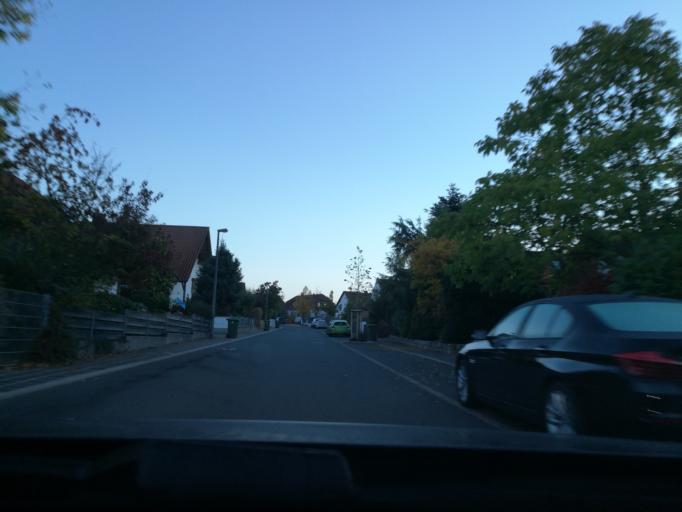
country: DE
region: Bavaria
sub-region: Regierungsbezirk Mittelfranken
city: Veitsbronn
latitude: 49.5130
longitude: 10.8947
